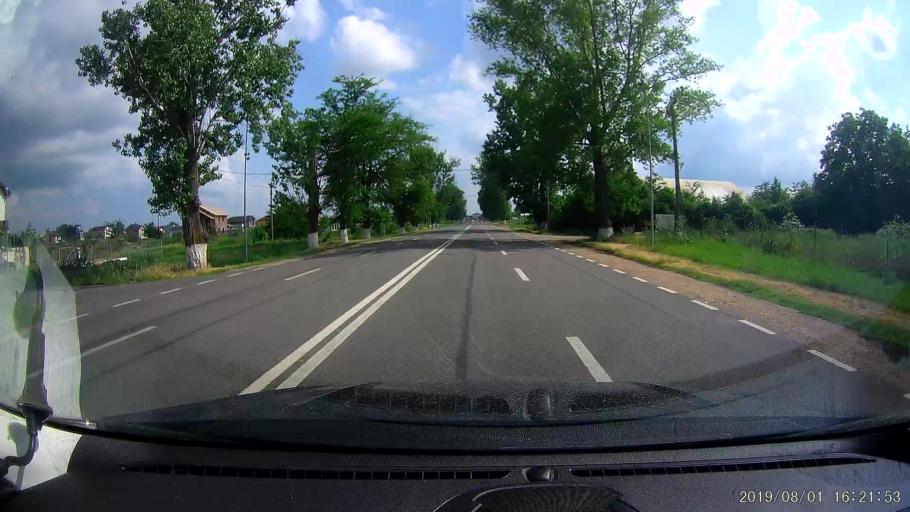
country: RO
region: Calarasi
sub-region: Municipiul Calarasi
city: Calarasi
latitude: 44.2108
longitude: 27.3388
